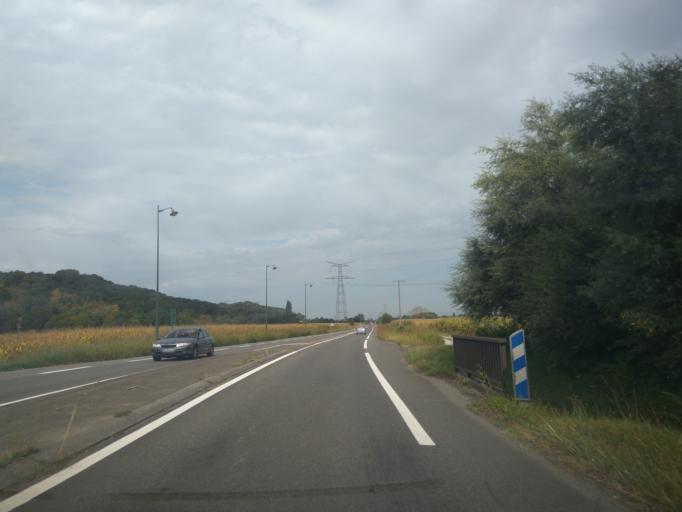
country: FR
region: Aquitaine
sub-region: Departement des Pyrenees-Atlantiques
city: Arbus
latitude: 43.3394
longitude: -0.5096
